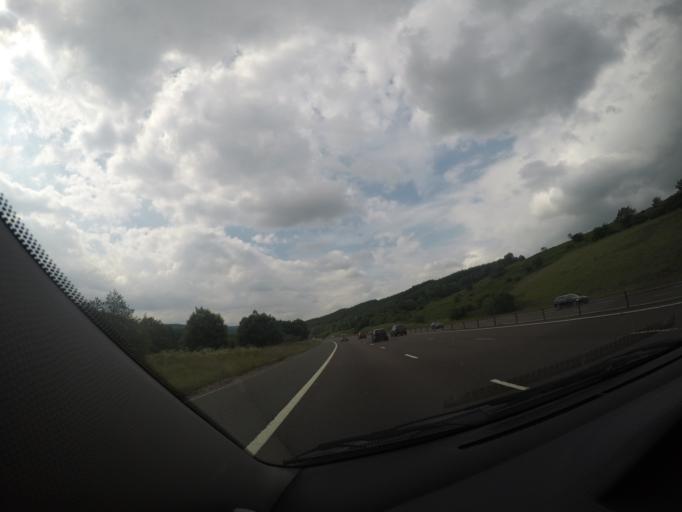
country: GB
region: Scotland
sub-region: Dumfries and Galloway
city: Moffat
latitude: 55.3384
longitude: -3.4837
